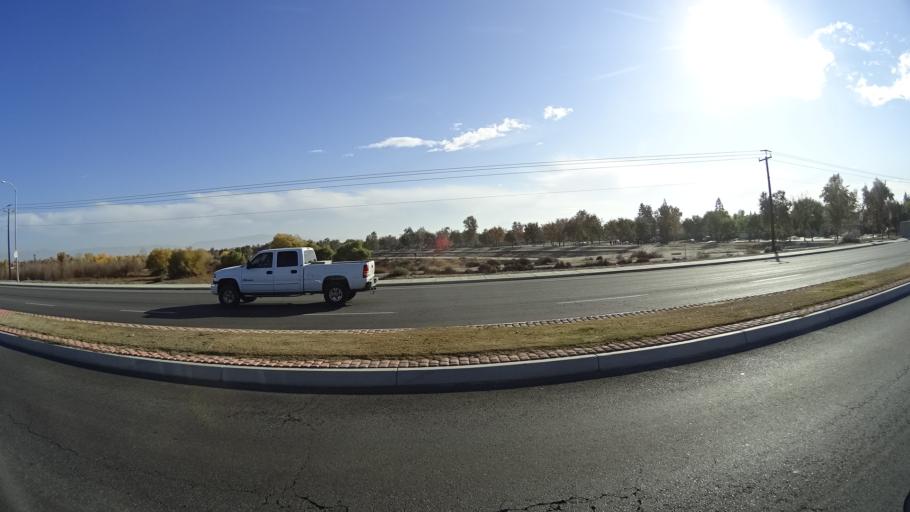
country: US
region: California
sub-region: Kern County
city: Rosedale
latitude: 35.3455
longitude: -119.1456
